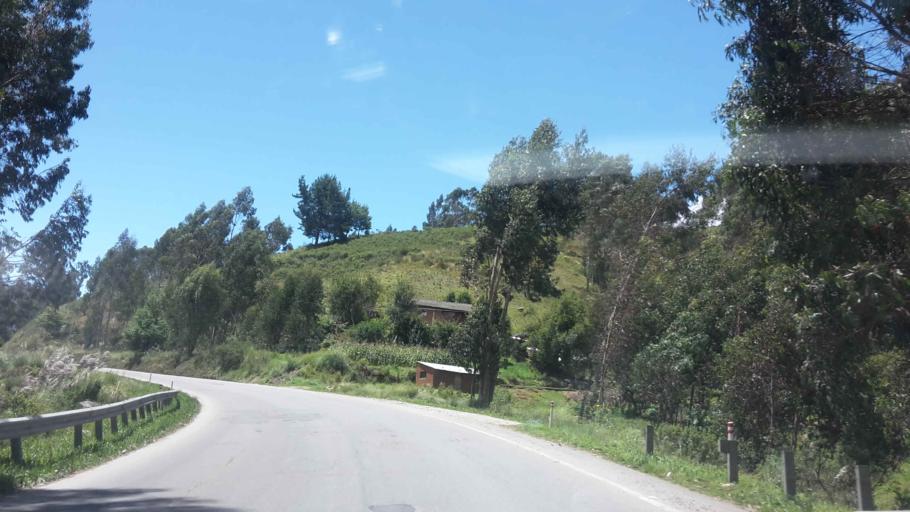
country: BO
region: Cochabamba
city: Colomi
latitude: -17.3214
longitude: -65.8733
